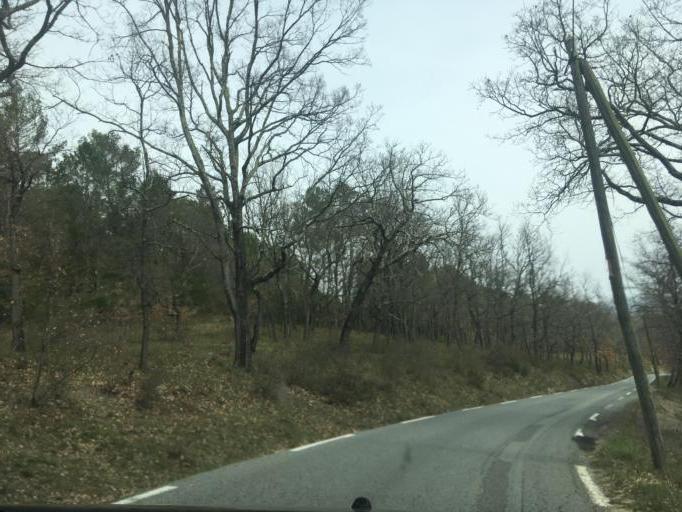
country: FR
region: Provence-Alpes-Cote d'Azur
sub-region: Departement du Var
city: Saint-Paul-en-Foret
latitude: 43.5808
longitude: 6.7260
